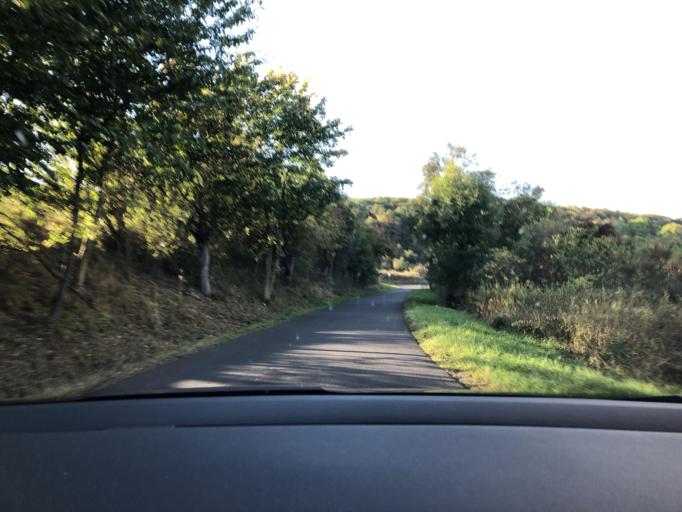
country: CZ
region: Ustecky
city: Zitenice
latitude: 50.5735
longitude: 14.1769
